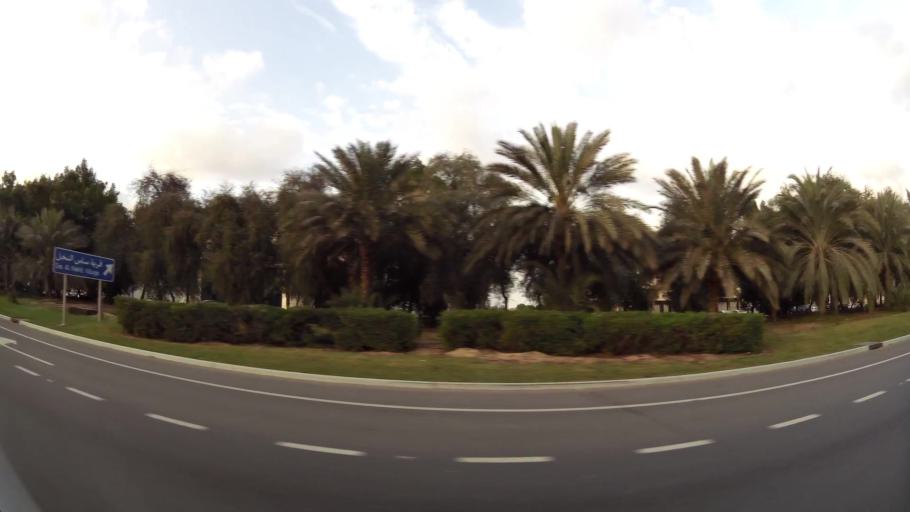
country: AE
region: Abu Dhabi
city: Abu Dhabi
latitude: 24.4083
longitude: 54.5184
